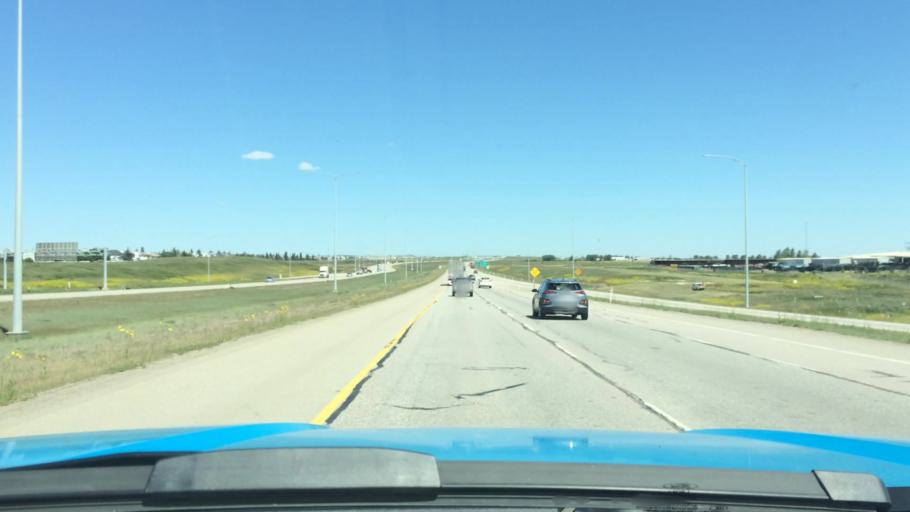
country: CA
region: Alberta
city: Chestermere
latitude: 51.0697
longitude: -113.9202
